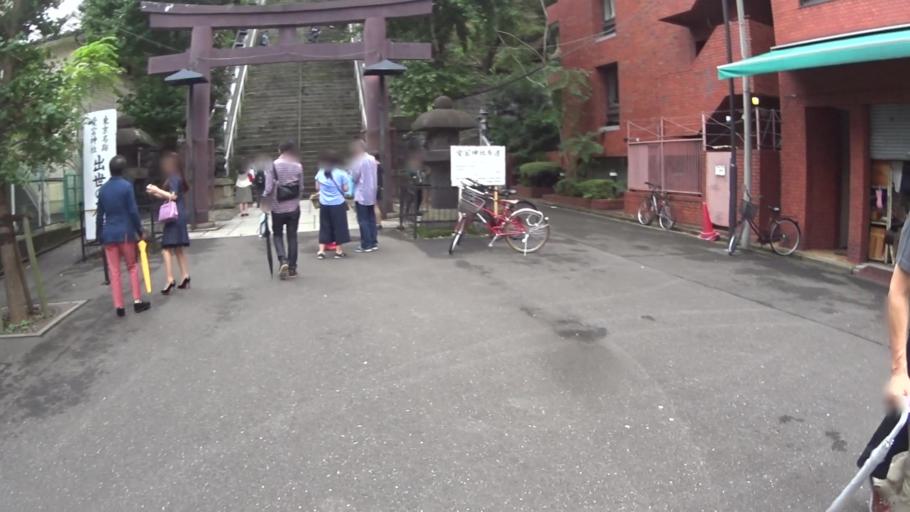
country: JP
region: Tokyo
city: Tokyo
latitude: 35.6648
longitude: 139.7497
